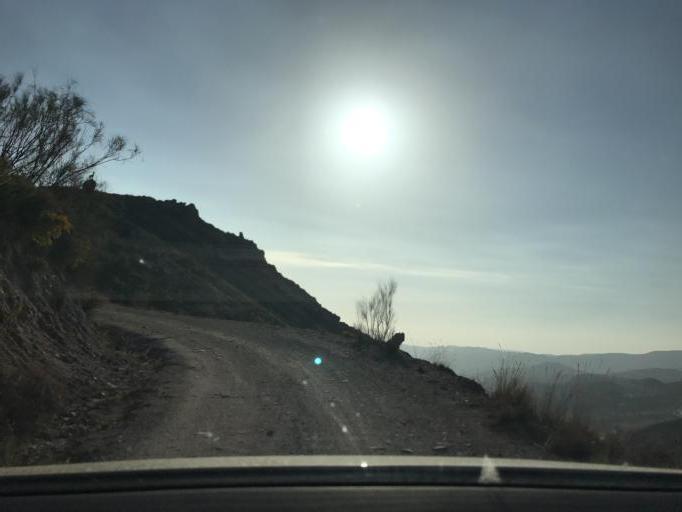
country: ES
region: Andalusia
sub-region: Provincia de Granada
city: Quentar
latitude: 37.1990
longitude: -3.4375
